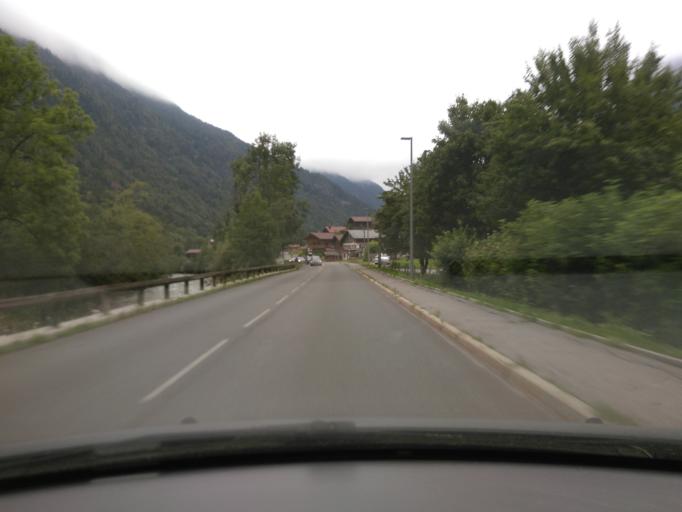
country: FR
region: Rhone-Alpes
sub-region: Departement de la Haute-Savoie
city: Saint-Jean-de-Sixt
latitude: 45.9588
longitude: 6.3878
